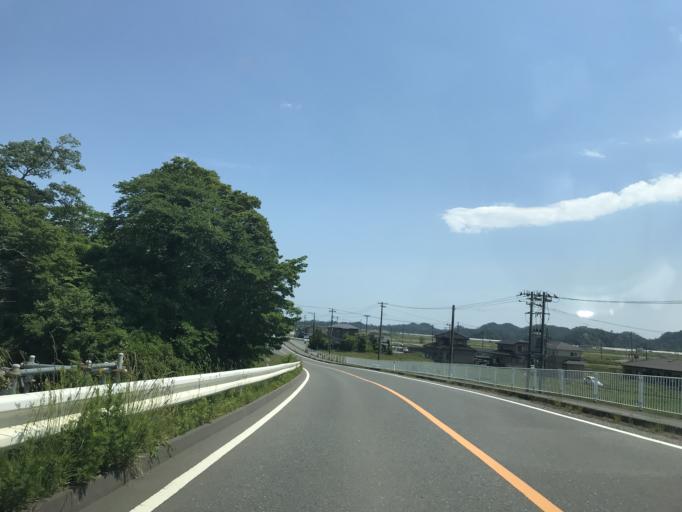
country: JP
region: Miyagi
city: Matsushima
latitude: 38.3722
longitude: 141.1407
